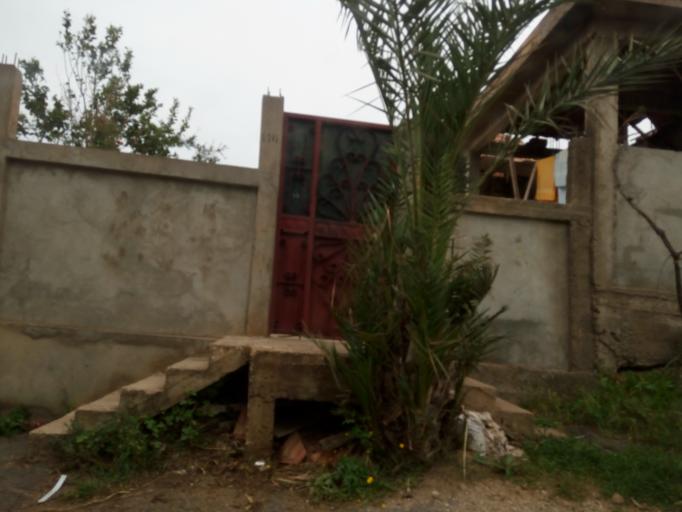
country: DZ
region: Tipaza
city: Tipasa
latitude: 36.5892
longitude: 2.4983
